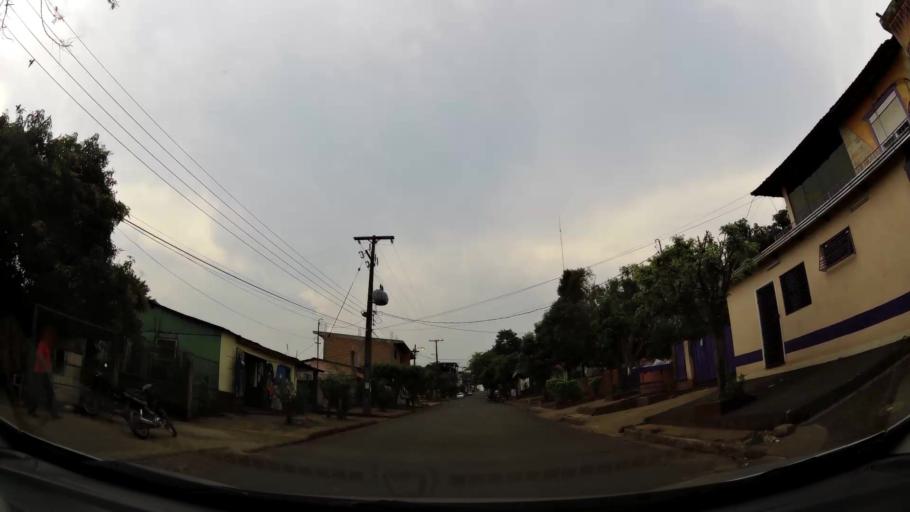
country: PY
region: Alto Parana
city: Presidente Franco
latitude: -25.5397
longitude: -54.6135
